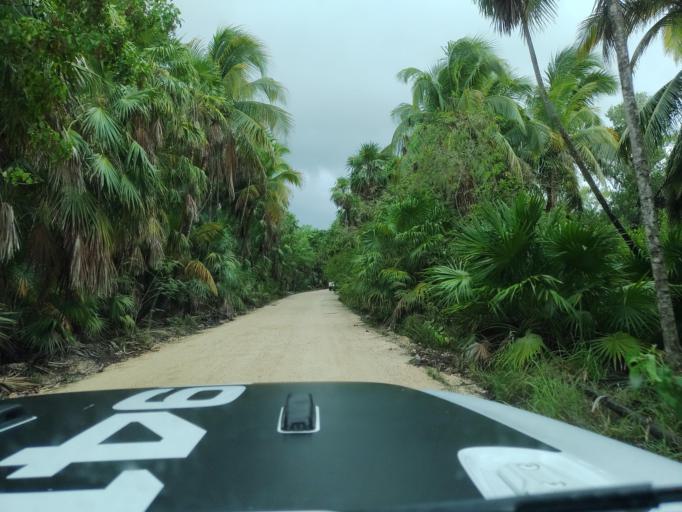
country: MX
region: Quintana Roo
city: Tulum
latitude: 20.0680
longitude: -87.4789
